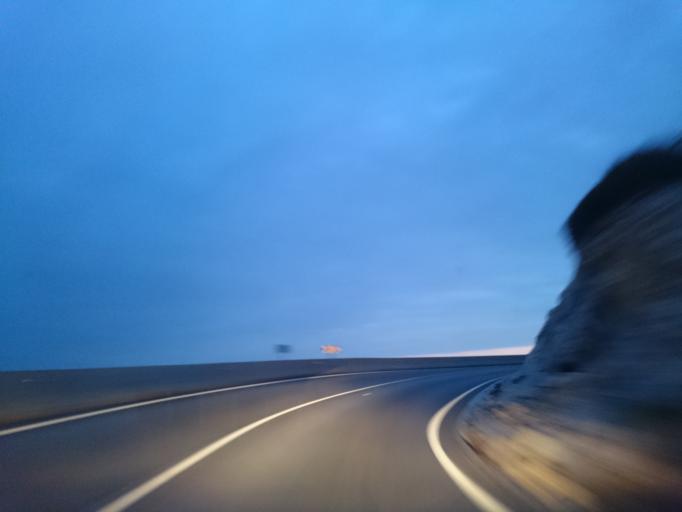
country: ES
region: Catalonia
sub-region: Provincia de Barcelona
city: Sitges
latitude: 41.2373
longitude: 1.8606
